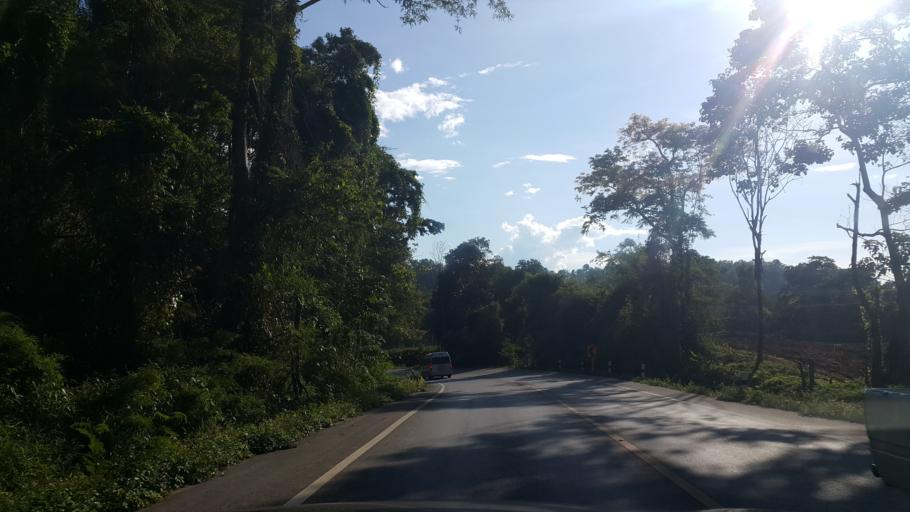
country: TH
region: Lampang
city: Wang Nuea
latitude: 19.0660
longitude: 99.7325
